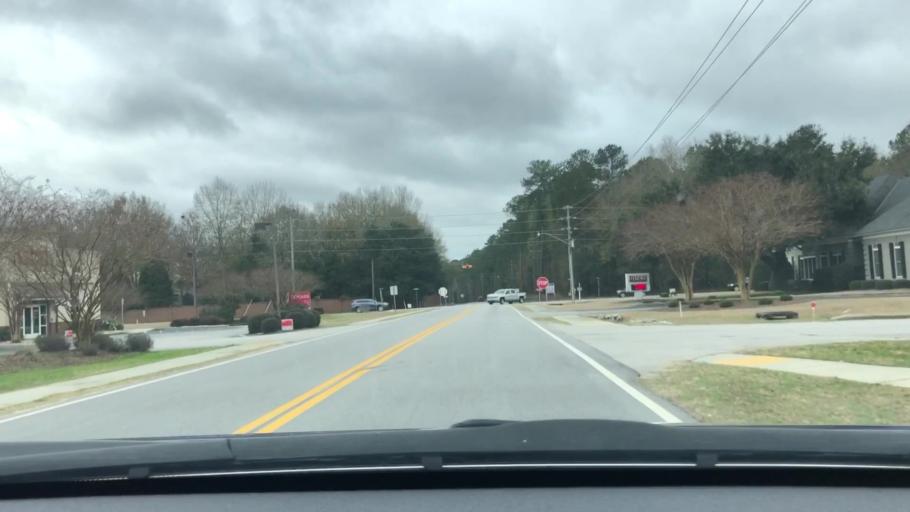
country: US
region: South Carolina
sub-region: Sumter County
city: Cherryvale
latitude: 33.9532
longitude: -80.4006
